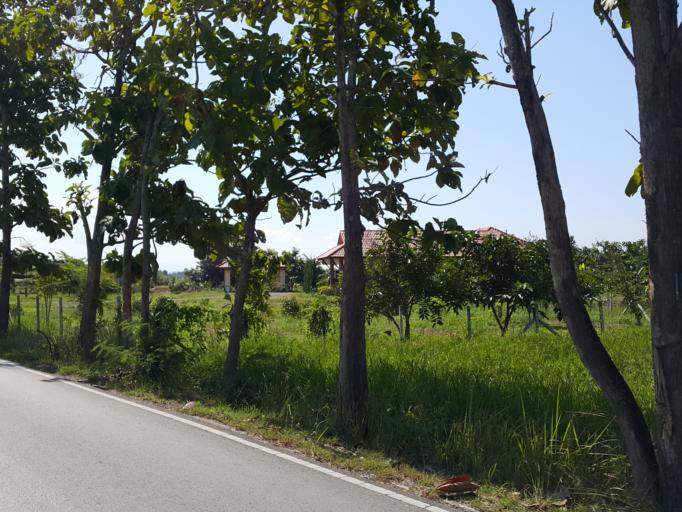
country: TH
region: Chiang Mai
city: San Sai
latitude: 18.8529
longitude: 99.1431
